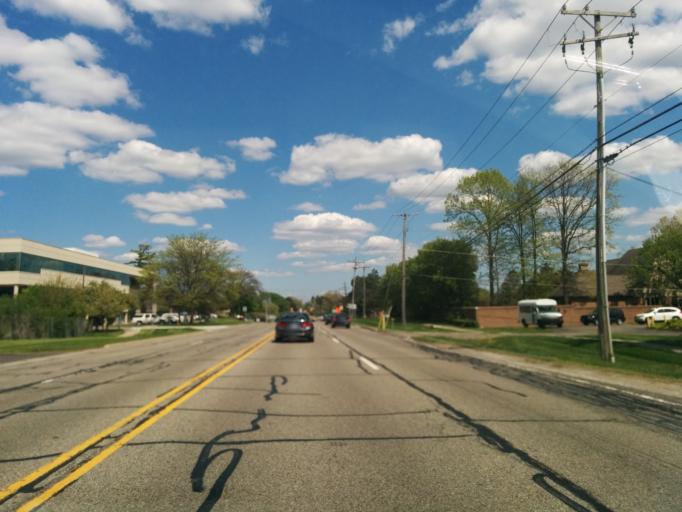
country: US
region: Michigan
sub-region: Oakland County
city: Franklin
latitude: 42.5144
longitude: -83.3357
